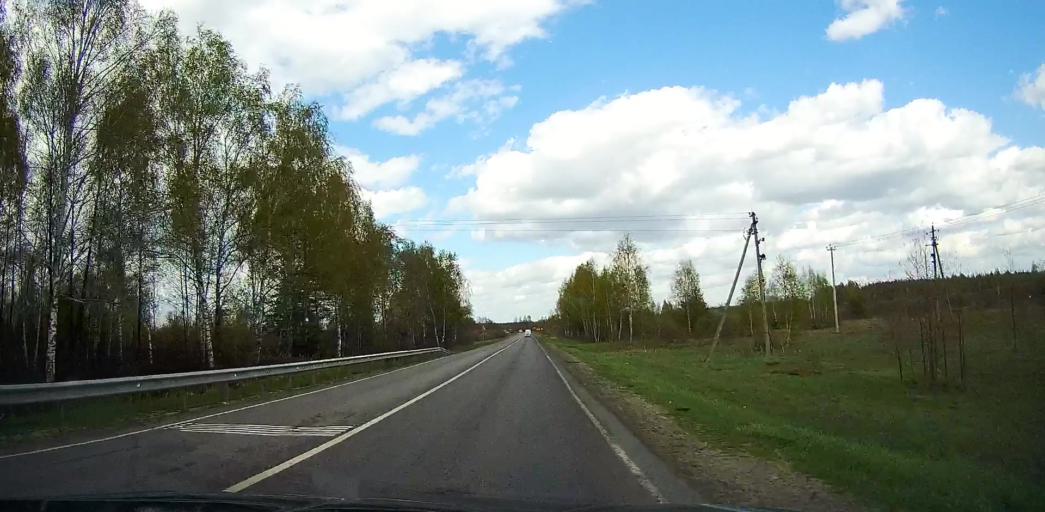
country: RU
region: Moskovskaya
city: Davydovo
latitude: 55.6298
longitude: 38.8637
